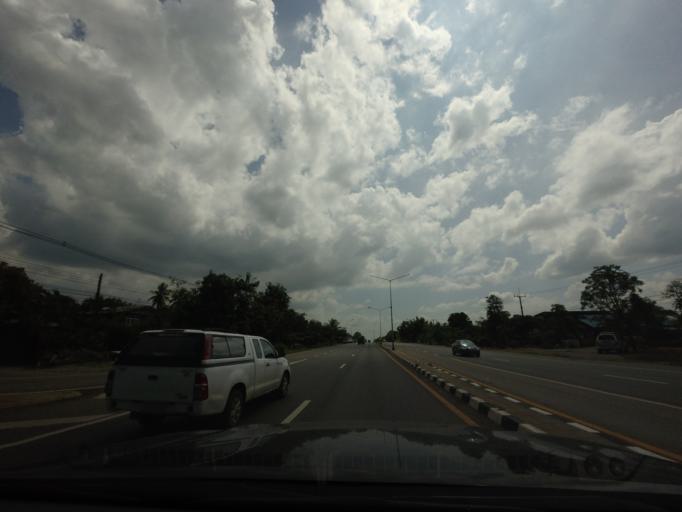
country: TH
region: Phetchabun
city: Phetchabun
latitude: 16.2212
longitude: 101.0891
